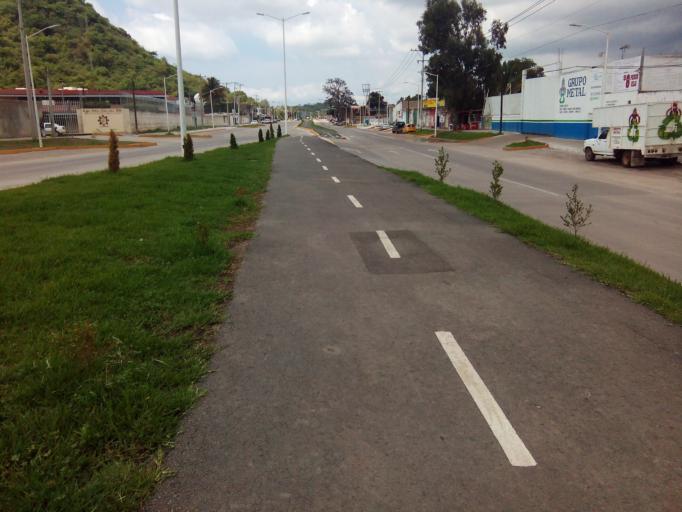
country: MX
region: Nayarit
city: Tepic
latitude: 21.5382
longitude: -104.8695
